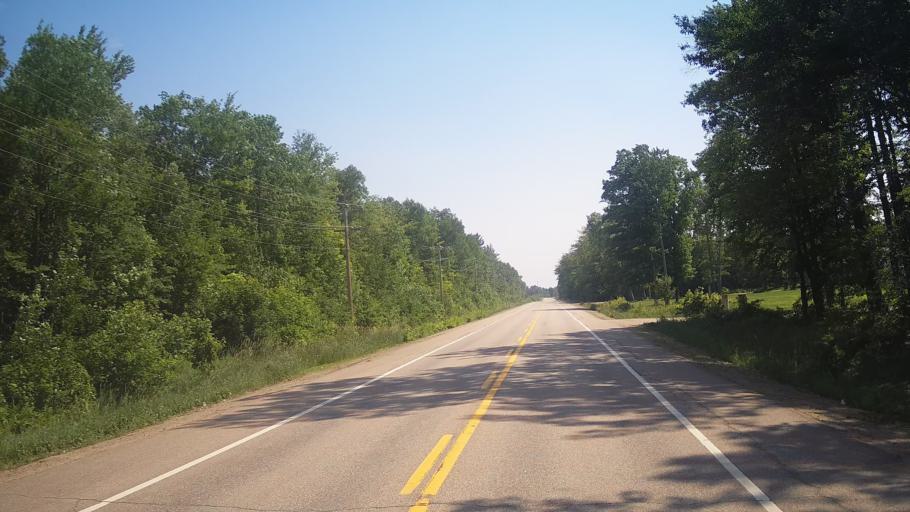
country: CA
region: Ontario
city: Pembroke
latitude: 45.8387
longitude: -77.0134
